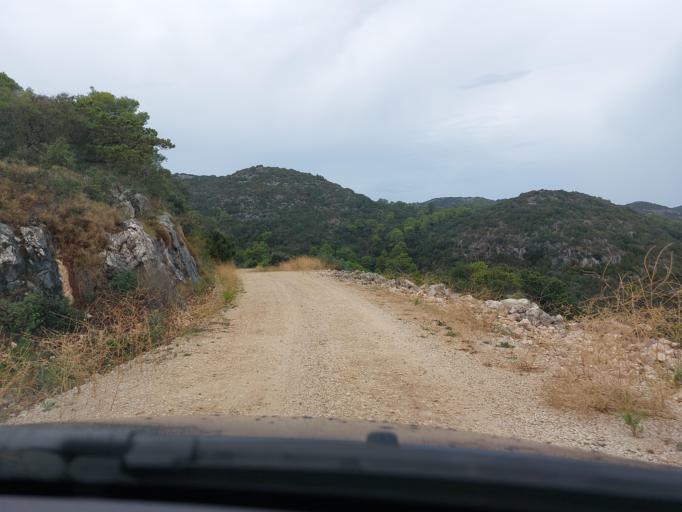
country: HR
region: Dubrovacko-Neretvanska
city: Smokvica
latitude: 42.7481
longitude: 16.9162
